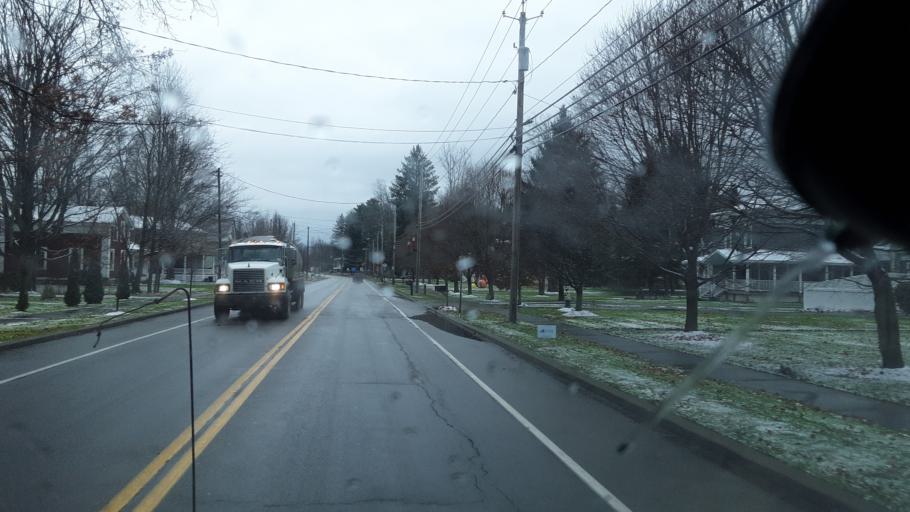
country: US
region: New York
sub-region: Cattaraugus County
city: Portville
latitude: 42.0414
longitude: -78.3437
